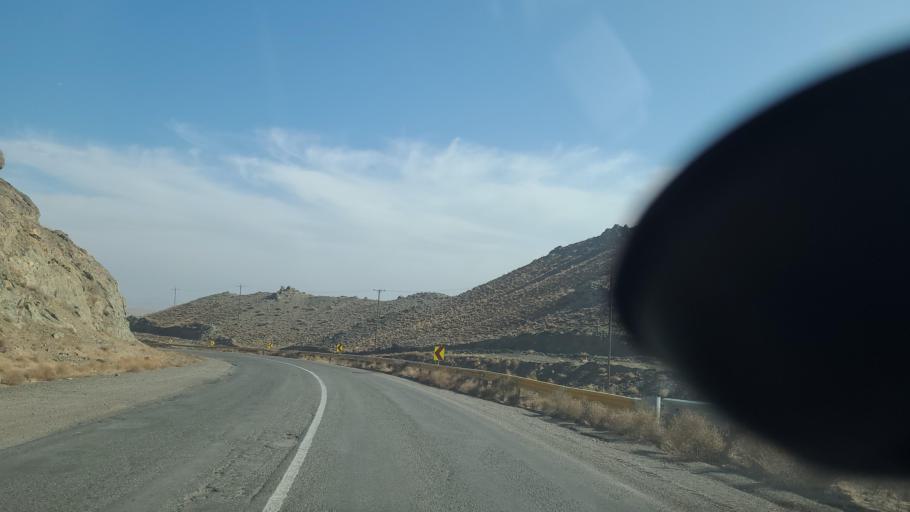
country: IR
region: Razavi Khorasan
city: Fariman
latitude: 35.5934
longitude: 59.7206
